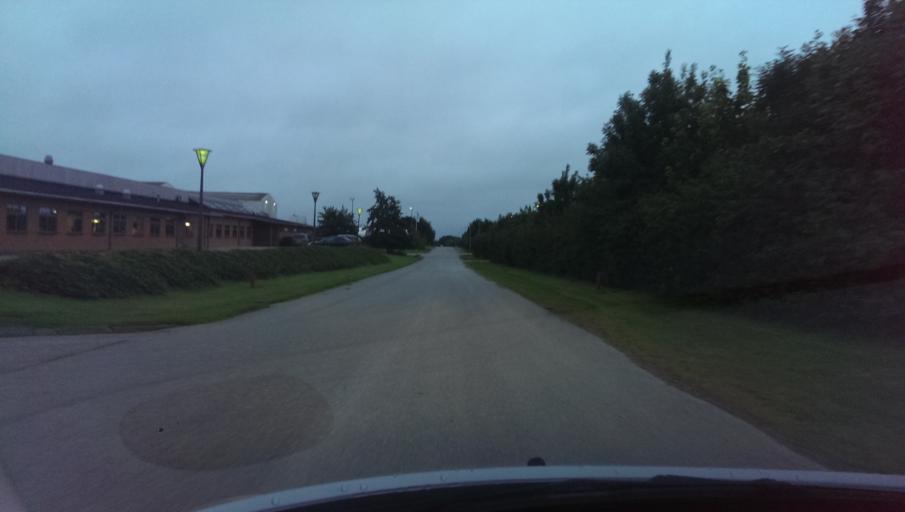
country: DK
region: South Denmark
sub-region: Varde Kommune
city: Olgod
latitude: 55.8165
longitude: 8.6368
